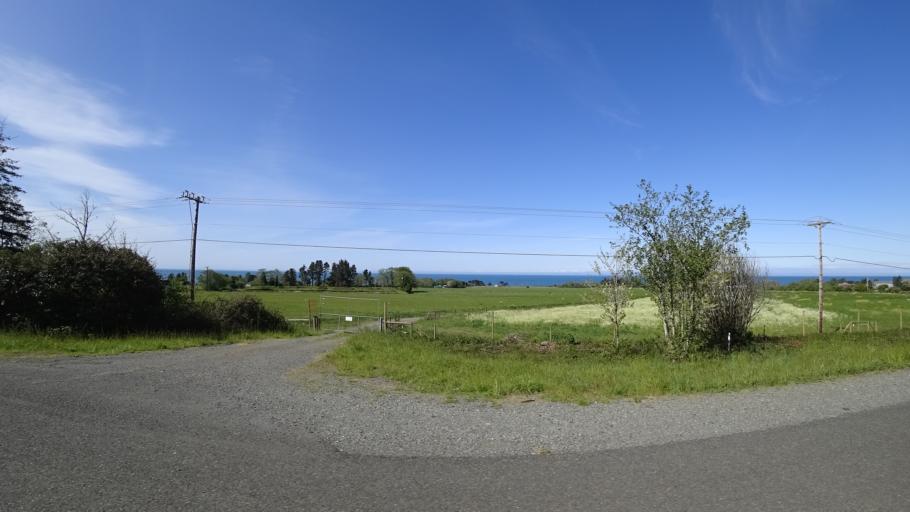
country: US
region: Oregon
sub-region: Curry County
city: Harbor
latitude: 42.0191
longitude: -124.2222
